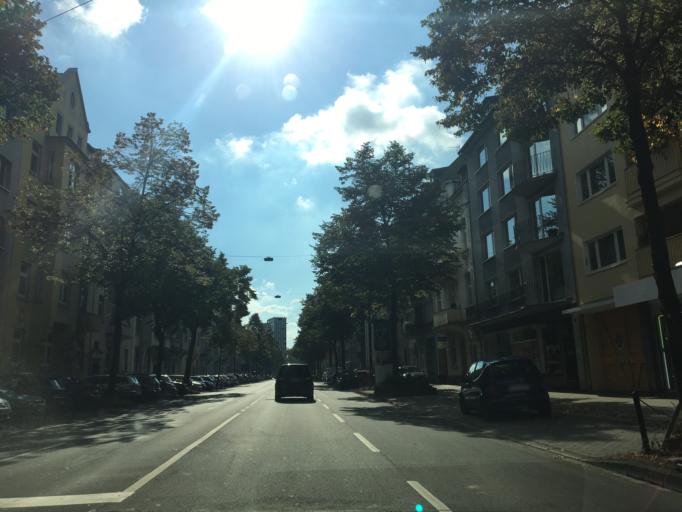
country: DE
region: North Rhine-Westphalia
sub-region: Regierungsbezirk Dusseldorf
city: Dusseldorf
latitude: 51.2043
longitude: 6.7767
